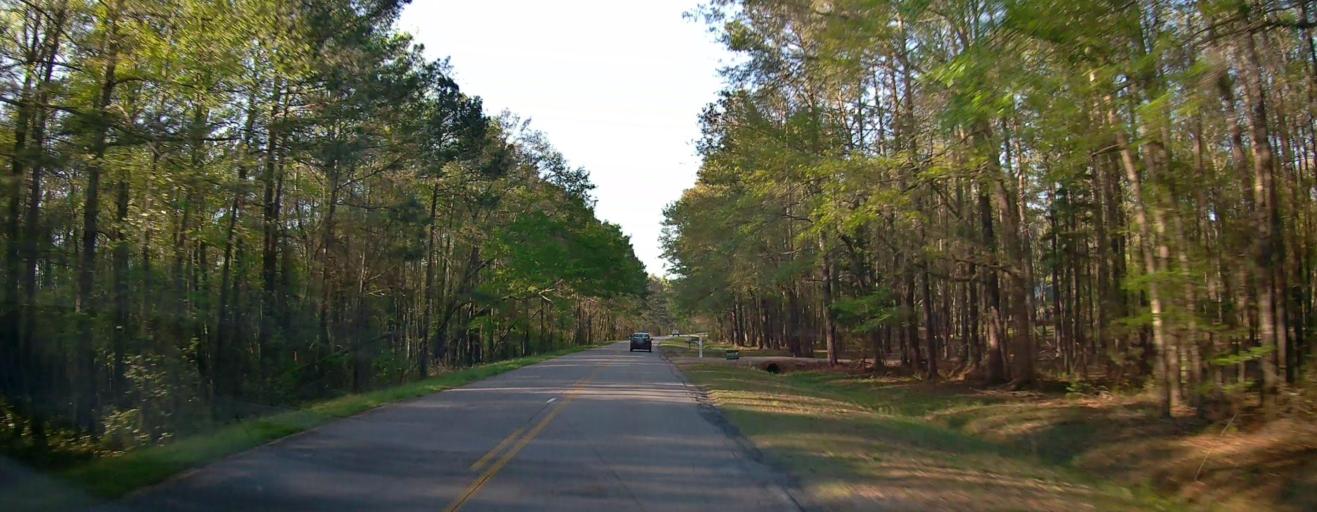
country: US
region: Georgia
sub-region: Butts County
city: Indian Springs
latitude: 33.2932
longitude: -83.8964
